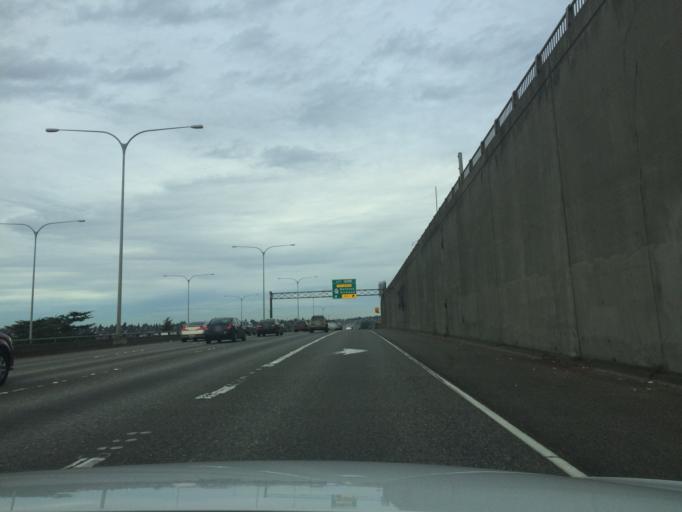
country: US
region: Washington
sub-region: King County
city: Seattle
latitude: 47.6374
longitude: -122.3226
